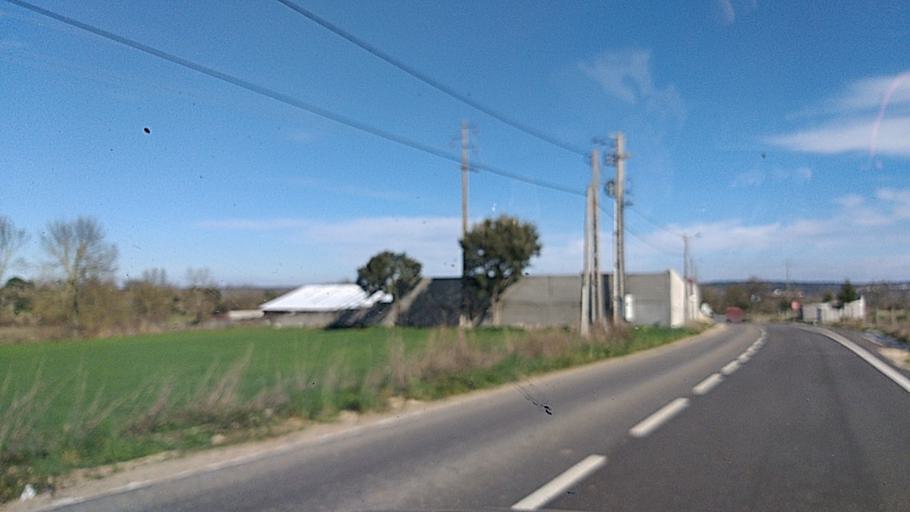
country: ES
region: Castille and Leon
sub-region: Provincia de Salamanca
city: Fuentes de Onoro
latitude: 40.5998
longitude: -6.9436
